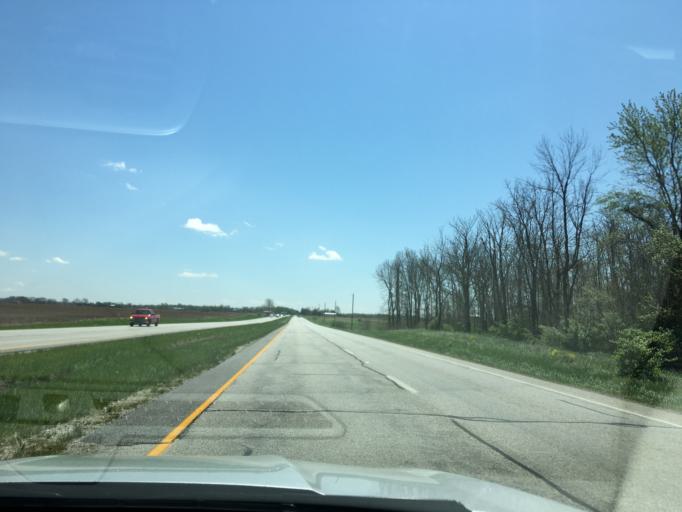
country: US
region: Indiana
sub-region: Tippecanoe County
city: Dayton
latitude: 40.3010
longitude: -86.7506
